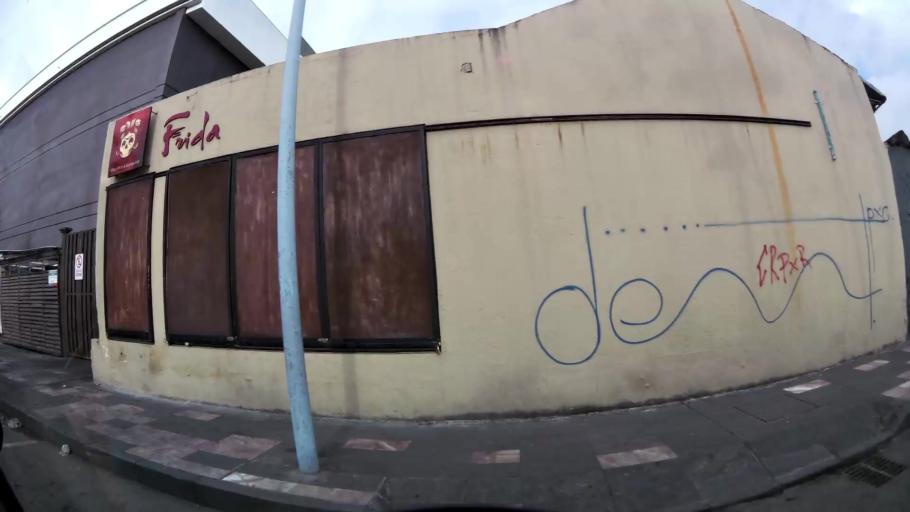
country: EC
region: Azuay
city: Cuenca
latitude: -2.9055
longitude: -79.0019
